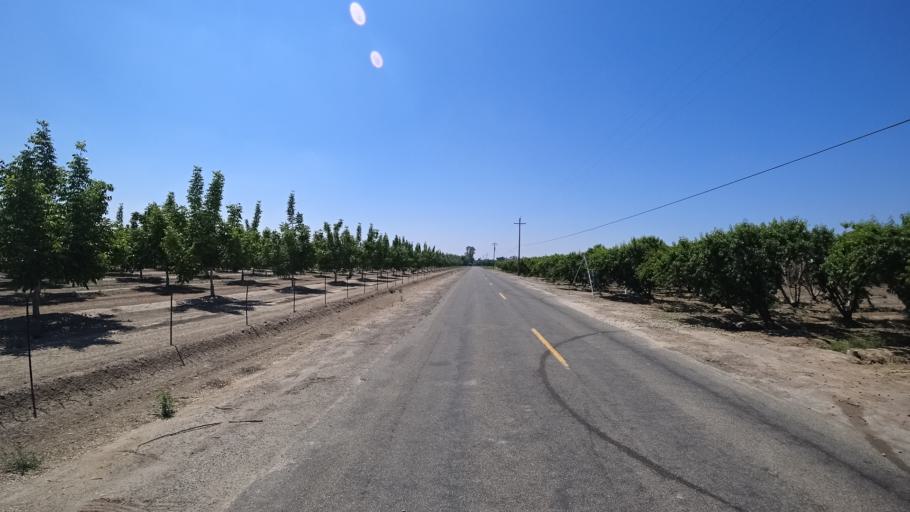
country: US
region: California
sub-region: Fresno County
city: Kingsburg
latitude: 36.4429
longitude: -119.6005
